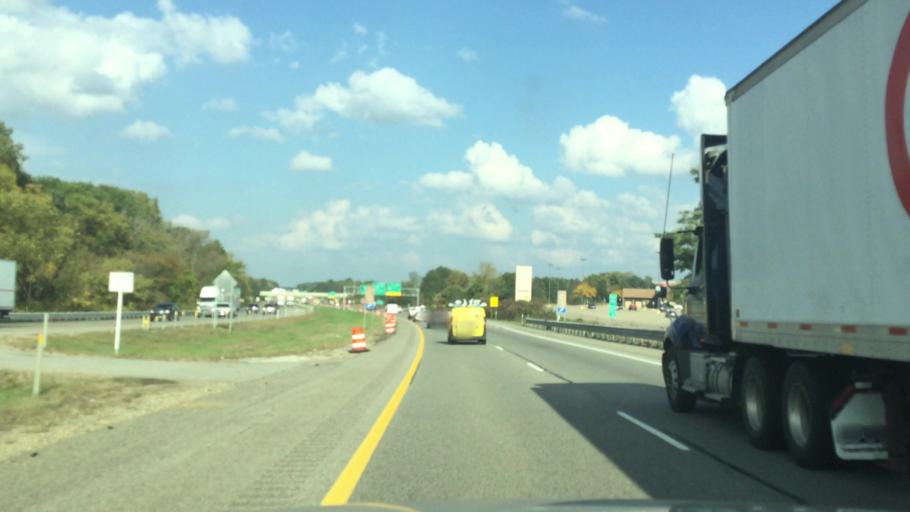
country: US
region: Michigan
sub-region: Calhoun County
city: Lakeview
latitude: 42.2638
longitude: -85.1865
